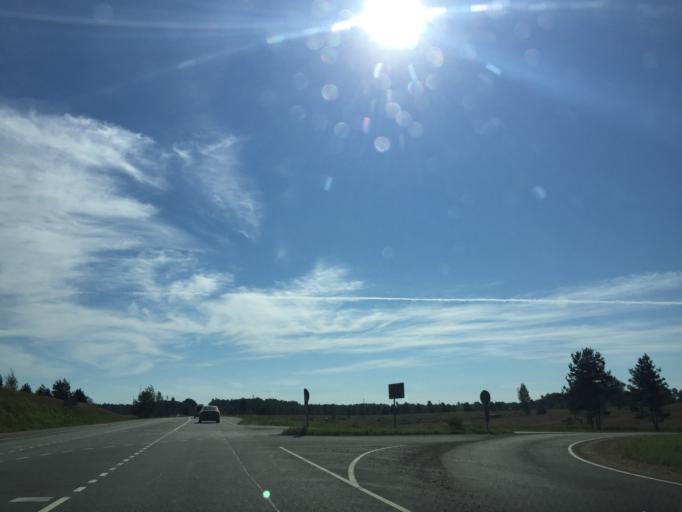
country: LV
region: Ikskile
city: Ikskile
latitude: 56.8854
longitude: 24.4951
